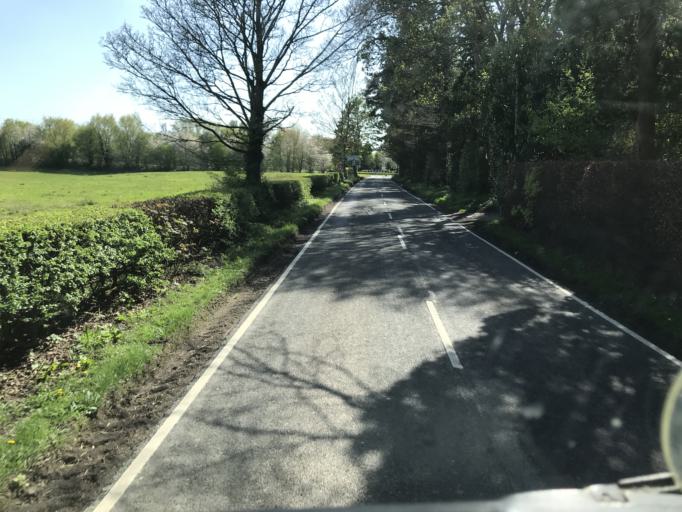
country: GB
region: England
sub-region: Cheshire East
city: Nantwich
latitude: 53.0803
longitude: -2.5226
